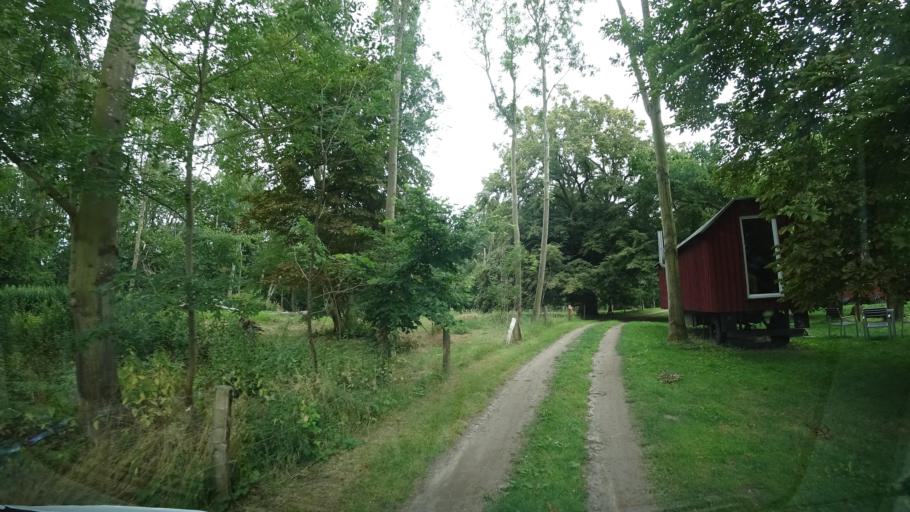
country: DE
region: Mecklenburg-Vorpommern
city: Rambin
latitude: 54.3264
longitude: 13.2096
